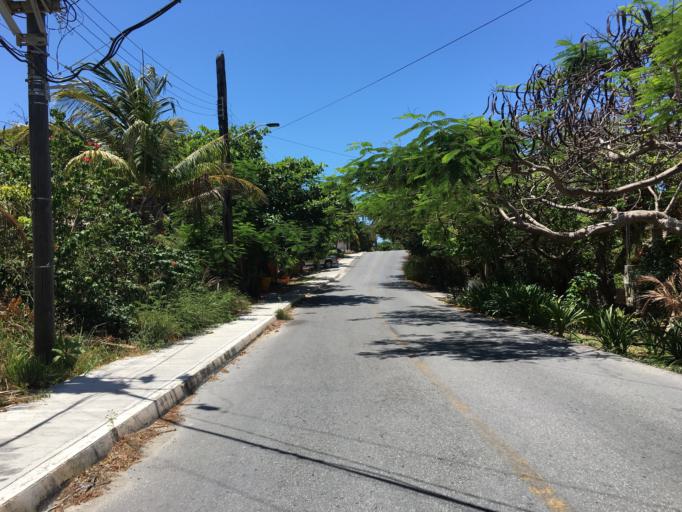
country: MX
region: Quintana Roo
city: Isla Mujeres
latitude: 21.2084
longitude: -86.7190
